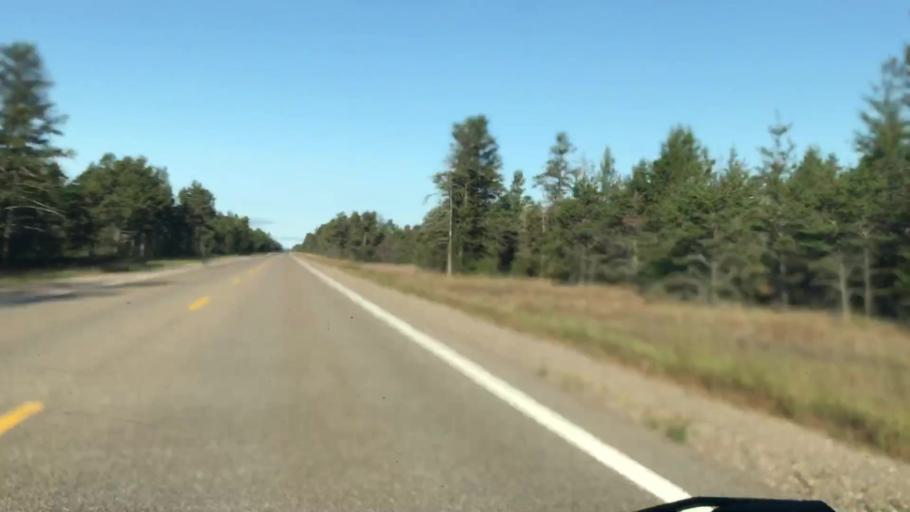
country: US
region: Michigan
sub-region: Mackinac County
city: Saint Ignace
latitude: 46.3586
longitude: -84.8323
